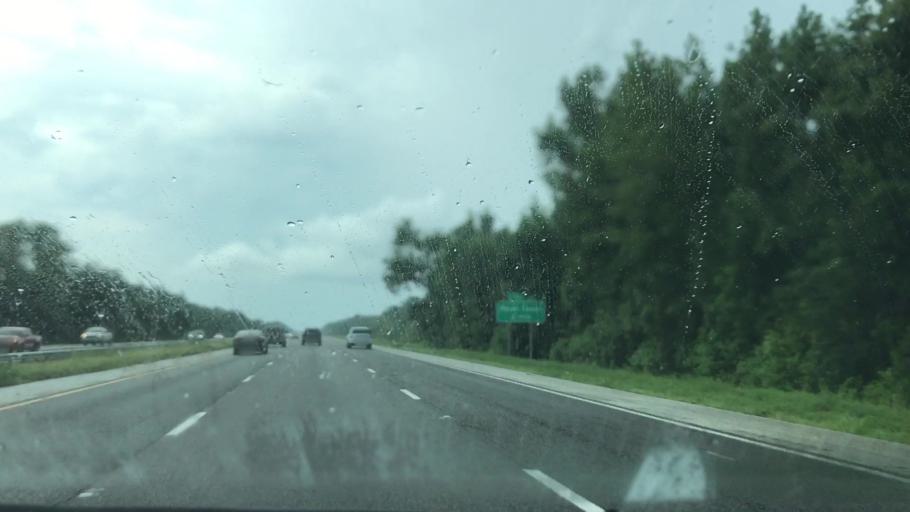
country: US
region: Florida
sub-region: Flagler County
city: Palm Coast
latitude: 29.6262
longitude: -81.2627
